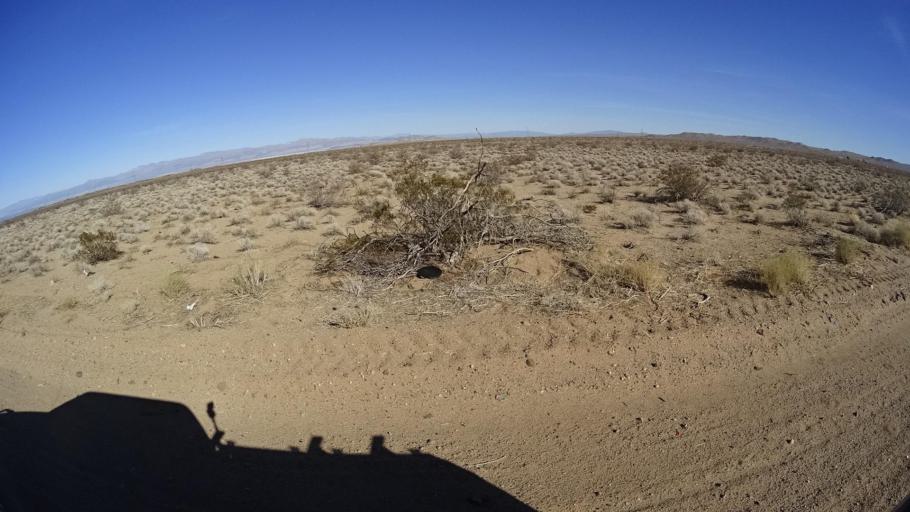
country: US
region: California
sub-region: Kern County
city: China Lake Acres
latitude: 35.5774
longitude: -117.7852
